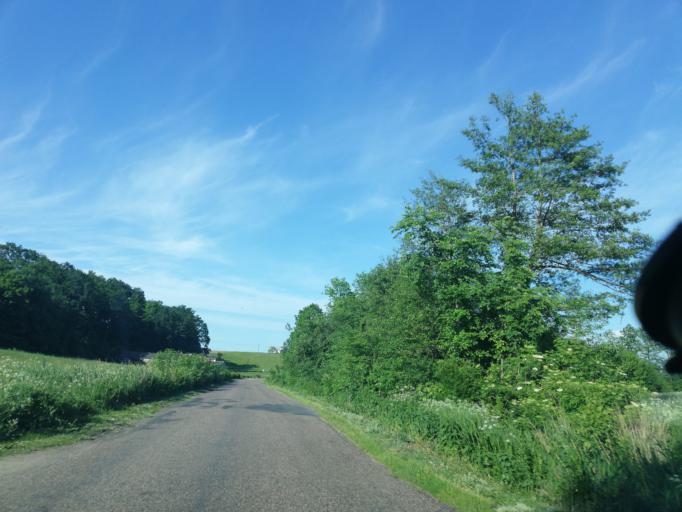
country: PL
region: Kujawsko-Pomorskie
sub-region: Powiat golubsko-dobrzynski
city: Golub-Dobrzyn
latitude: 53.0373
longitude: 19.0818
